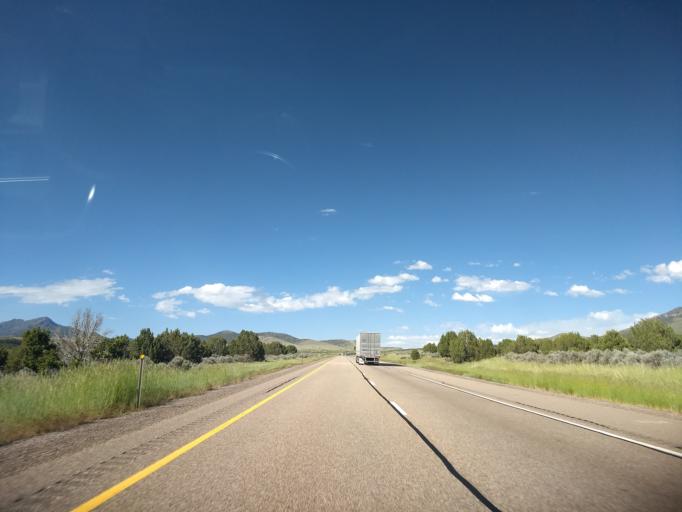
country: US
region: Utah
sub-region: Millard County
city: Fillmore
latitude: 39.1644
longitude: -112.2190
